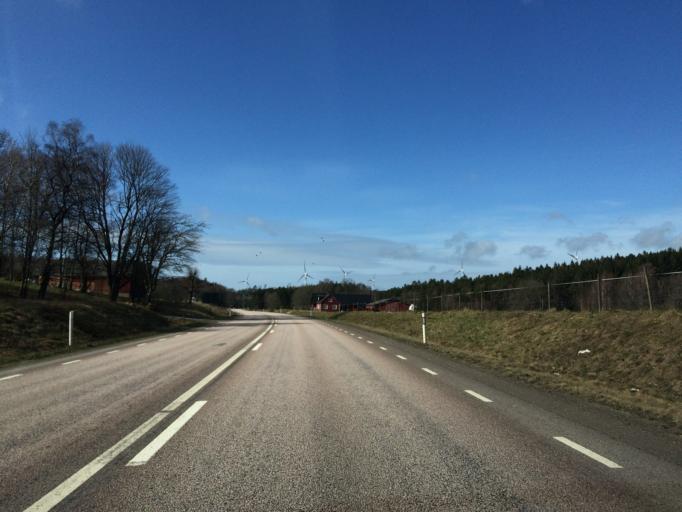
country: SE
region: Halland
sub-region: Laholms Kommun
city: Knared
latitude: 56.5268
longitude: 13.2439
